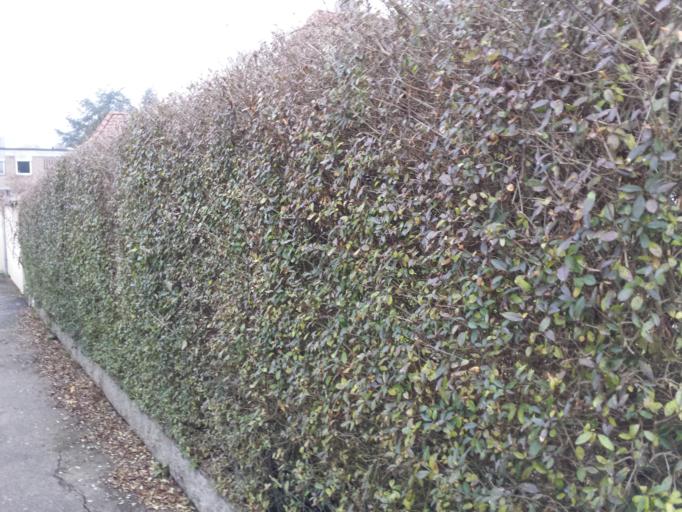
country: DE
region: Baden-Wuerttemberg
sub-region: Regierungsbezirk Stuttgart
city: Sindelfingen
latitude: 48.7106
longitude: 9.0104
